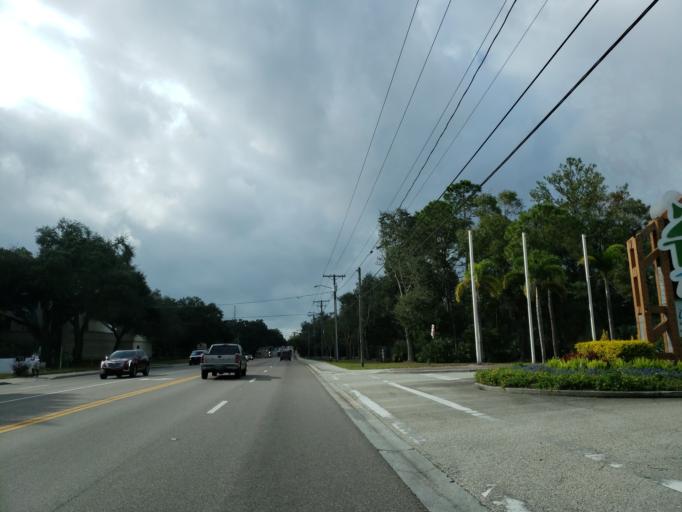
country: US
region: Florida
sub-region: Hillsborough County
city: Egypt Lake-Leto
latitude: 28.0108
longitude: -82.4687
